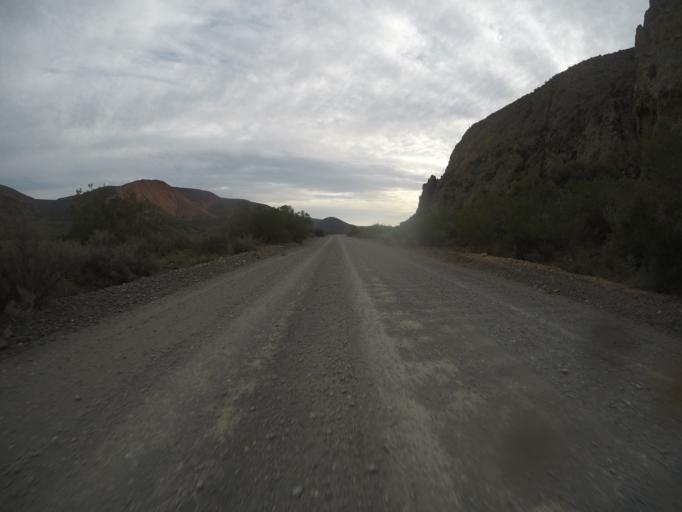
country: ZA
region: Eastern Cape
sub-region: Cacadu District Municipality
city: Willowmore
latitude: -33.5232
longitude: 23.6562
